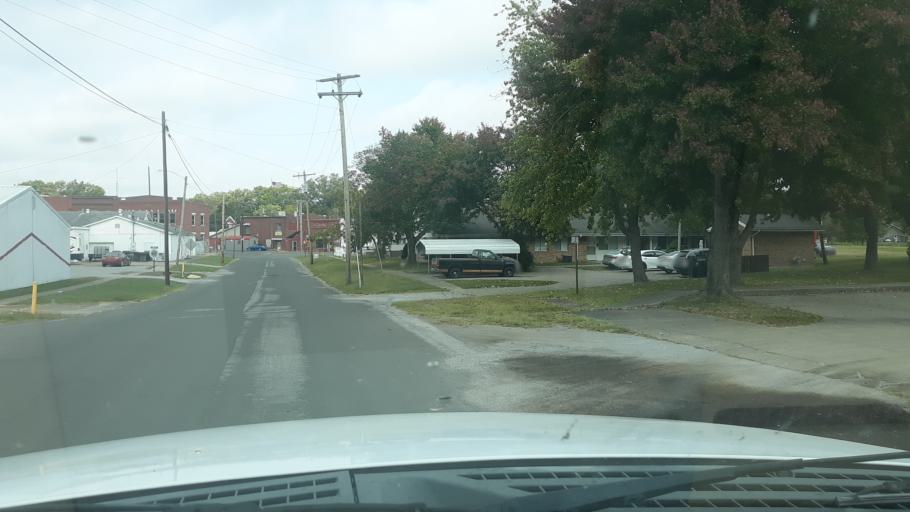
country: US
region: Illinois
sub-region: Saline County
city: Eldorado
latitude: 37.8132
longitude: -88.4365
